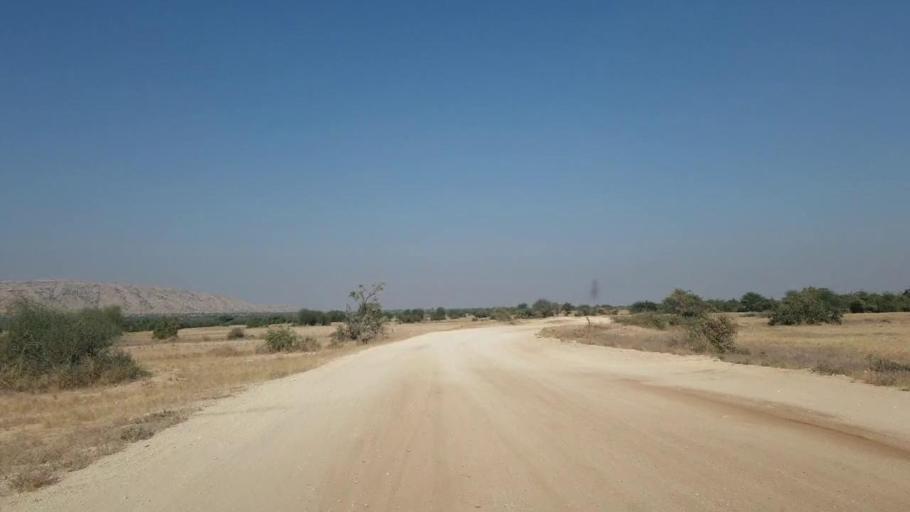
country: PK
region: Sindh
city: Jamshoro
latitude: 25.2675
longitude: 67.8052
